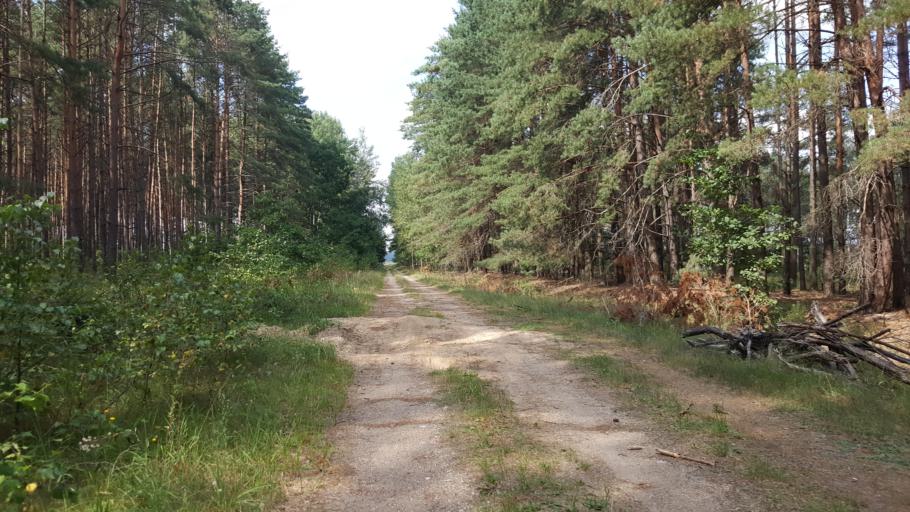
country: PL
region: Podlasie
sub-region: Powiat hajnowski
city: Hajnowka
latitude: 52.5730
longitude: 23.5883
